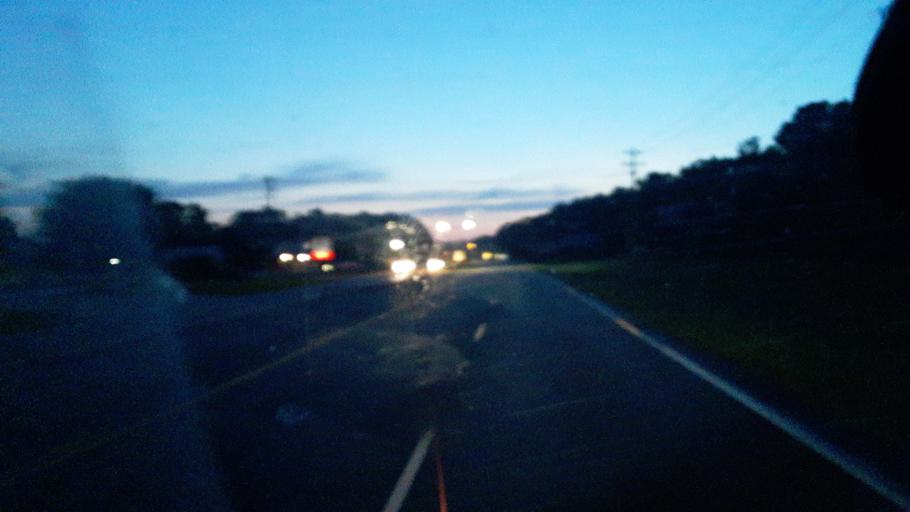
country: US
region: South Carolina
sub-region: Horry County
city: Little River
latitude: 33.8782
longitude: -78.6090
